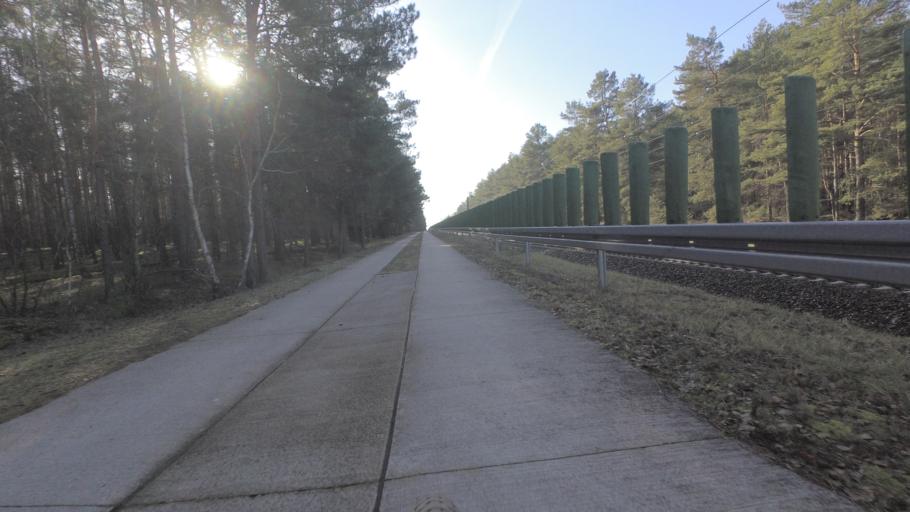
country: DE
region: Brandenburg
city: Trebbin
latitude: 52.1602
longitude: 13.2208
